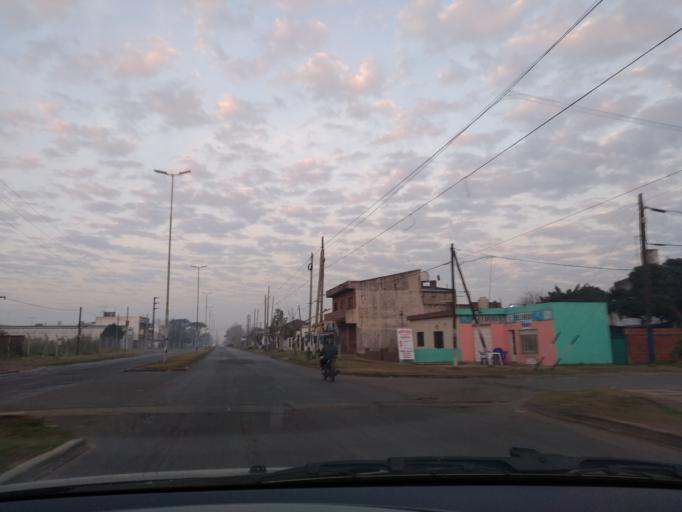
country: AR
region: Buenos Aires
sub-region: Partido de La Plata
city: La Plata
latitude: -34.9749
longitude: -57.9886
